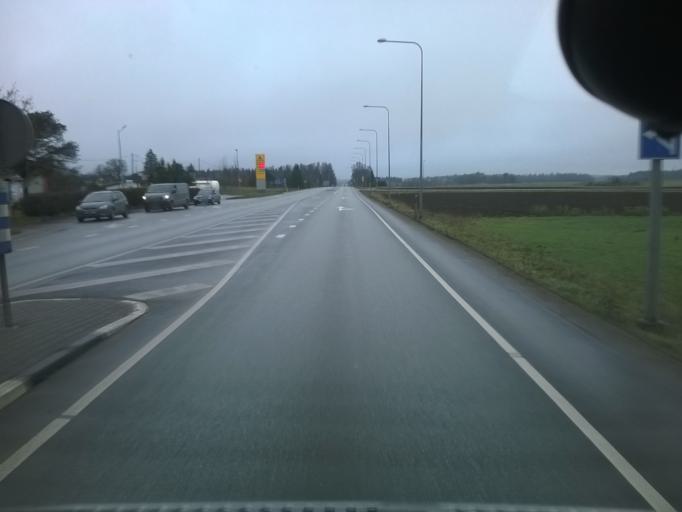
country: EE
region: Harju
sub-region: Saku vald
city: Saku
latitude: 59.2693
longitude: 24.7412
